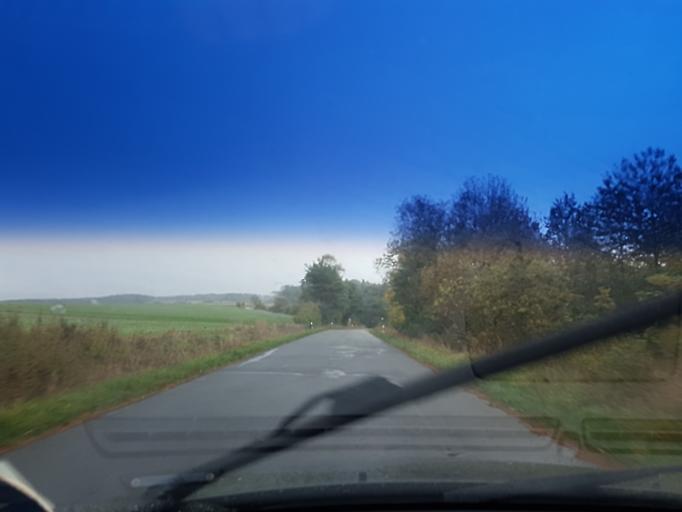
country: DE
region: Bavaria
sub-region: Regierungsbezirk Mittelfranken
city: Markt Taschendorf
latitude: 49.7574
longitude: 10.5457
